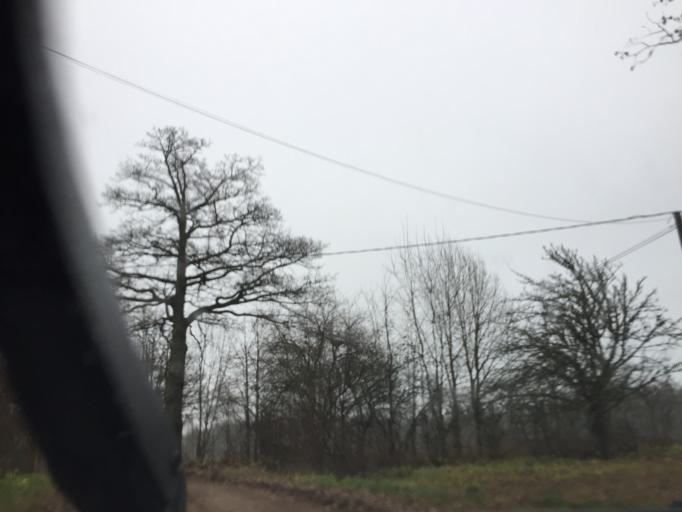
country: LV
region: Koceni
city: Koceni
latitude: 57.5108
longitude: 25.3312
